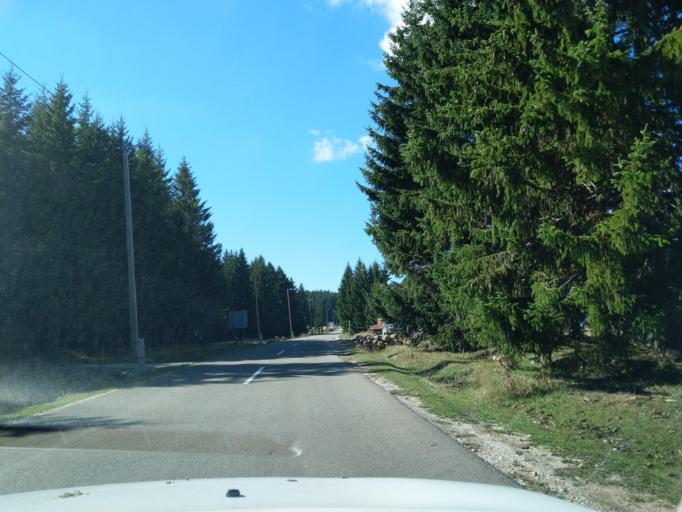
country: RS
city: Sokolovica
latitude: 43.2765
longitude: 20.3435
